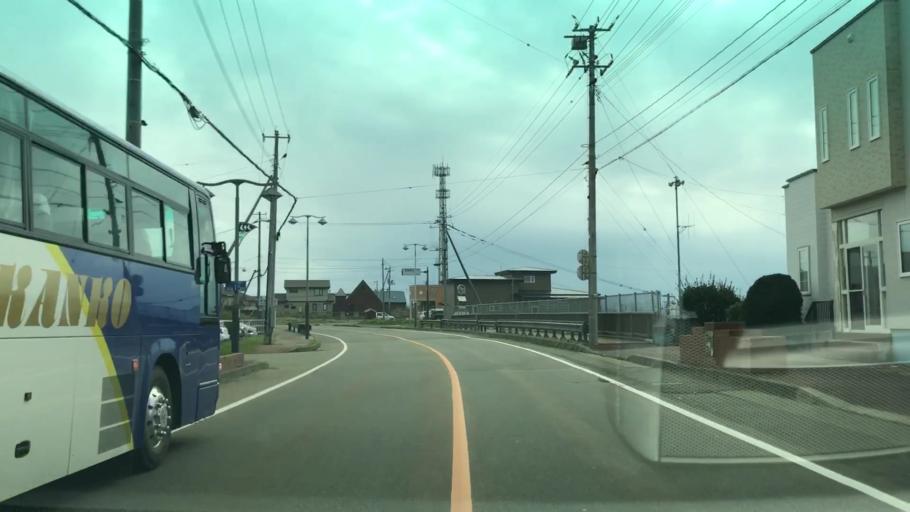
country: JP
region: Hokkaido
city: Shizunai-furukawacho
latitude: 42.0130
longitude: 143.1486
